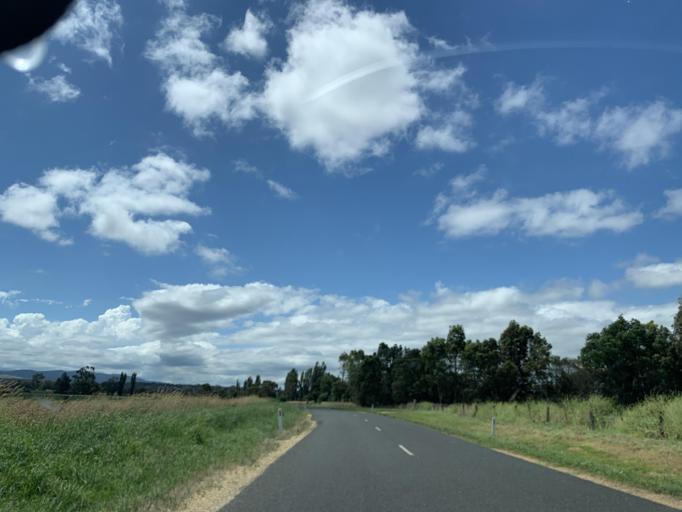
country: AU
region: Victoria
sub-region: Wellington
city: Heyfield
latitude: -37.9886
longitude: 146.6932
